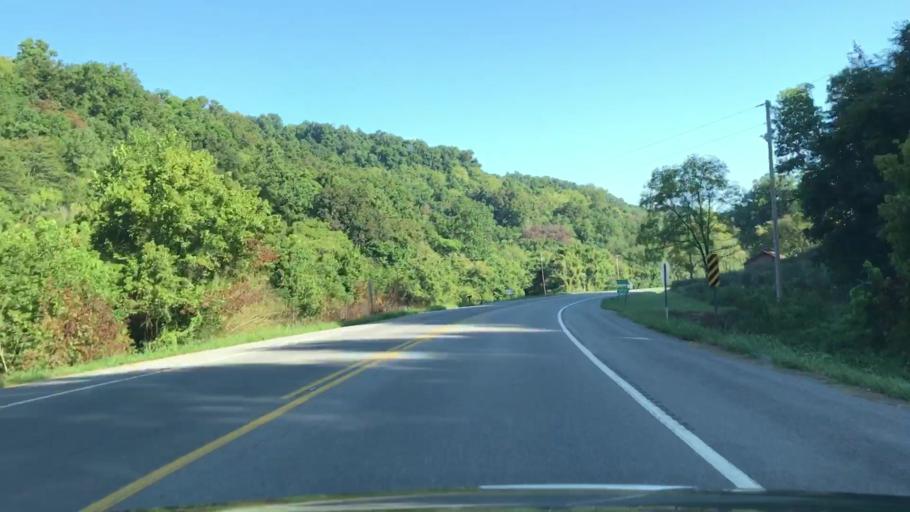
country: US
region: Tennessee
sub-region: Jackson County
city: Gainesboro
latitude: 36.3238
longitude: -85.6581
